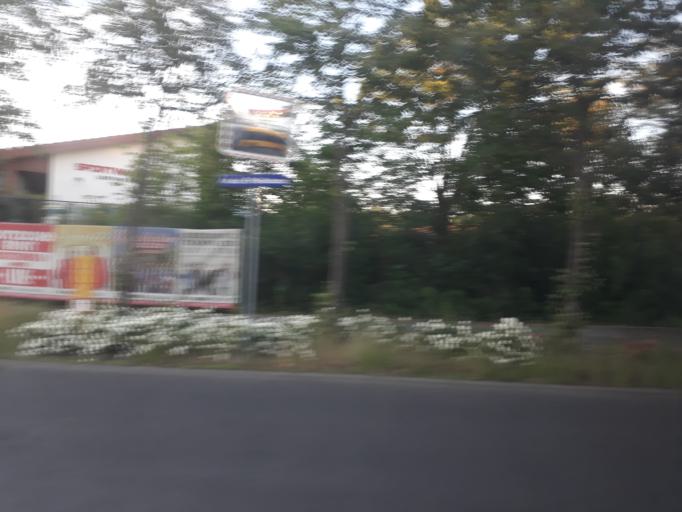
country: DE
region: Saxony
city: Radeberg
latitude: 51.0683
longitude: 13.8861
